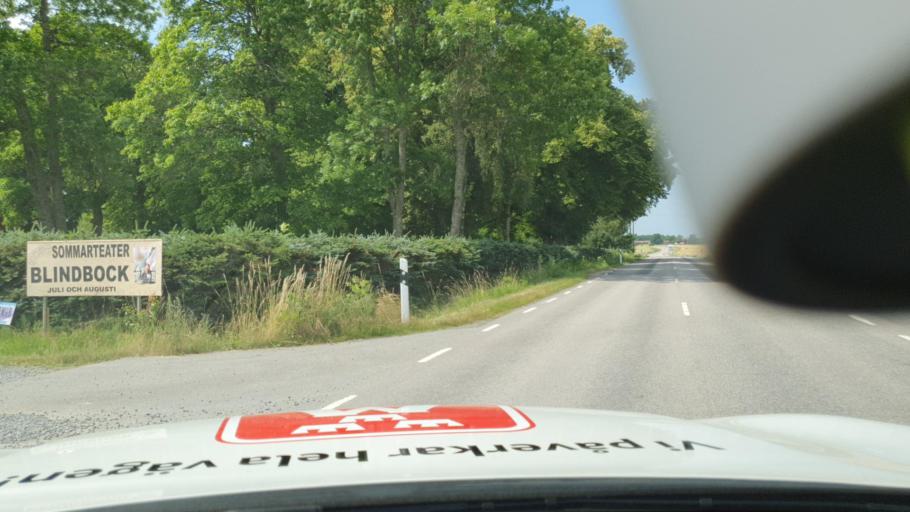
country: SE
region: Vaestra Goetaland
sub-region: Lidkopings Kommun
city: Lidkoping
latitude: 58.5216
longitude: 13.0998
